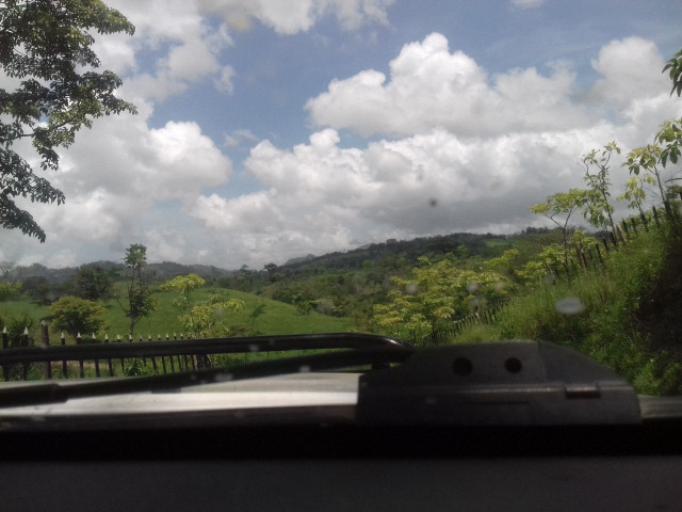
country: NI
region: Matagalpa
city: Rio Blanco
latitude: 12.9825
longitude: -85.3736
